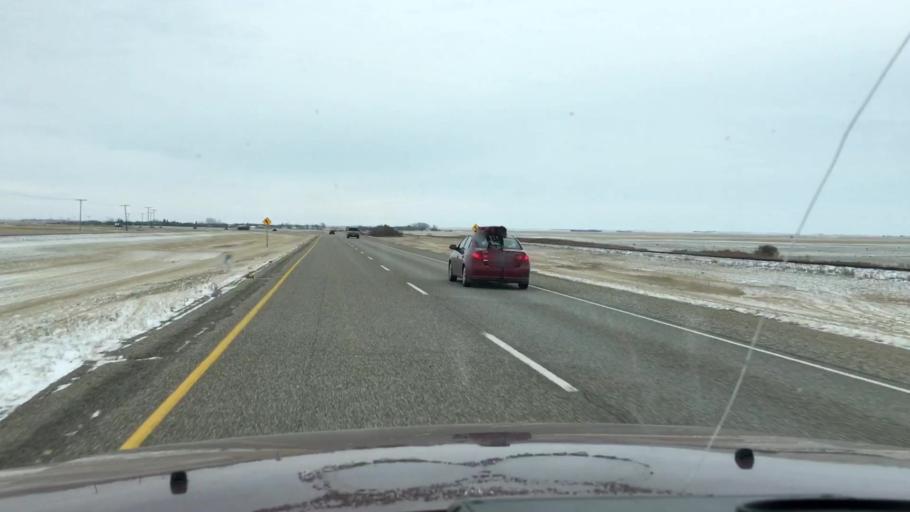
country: CA
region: Saskatchewan
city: Watrous
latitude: 51.1749
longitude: -105.9343
